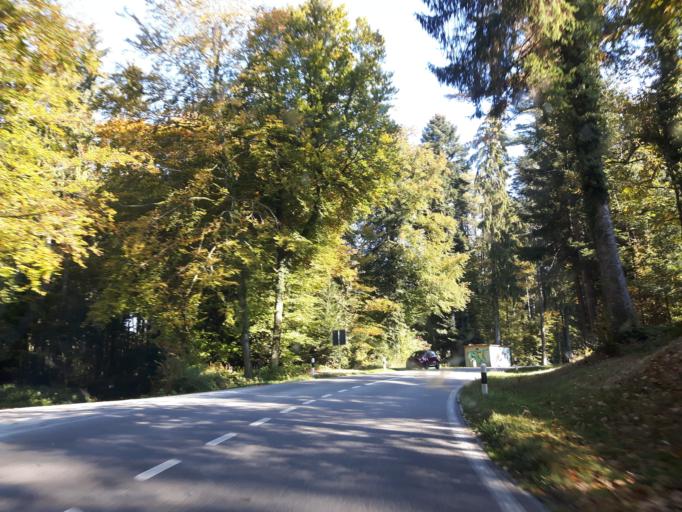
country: CH
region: Bern
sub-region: Oberaargau
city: Roggwil
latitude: 47.2460
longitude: 7.8386
